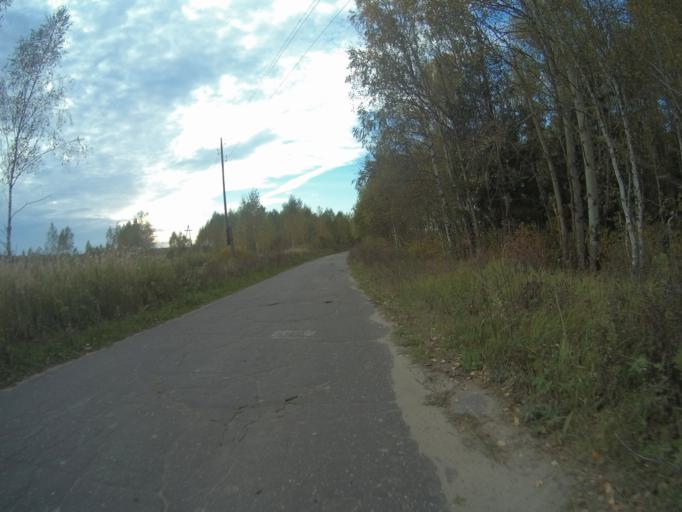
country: RU
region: Vladimir
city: Golovino
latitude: 55.9711
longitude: 40.3952
